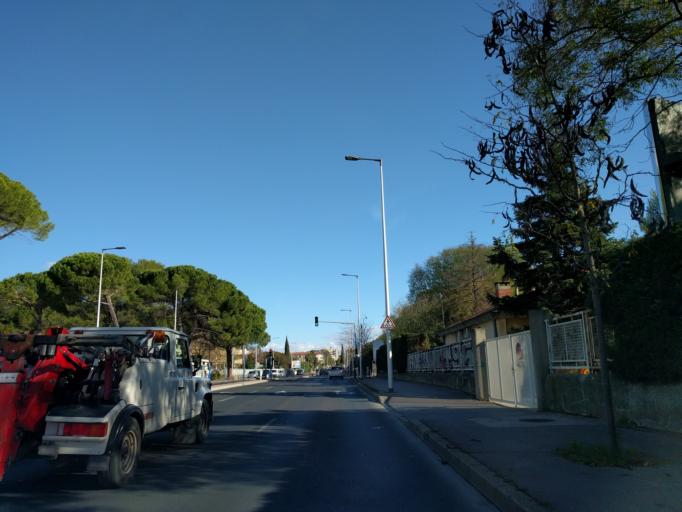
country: FR
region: Languedoc-Roussillon
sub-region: Departement de l'Herault
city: Montpellier
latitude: 43.6219
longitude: 3.8594
